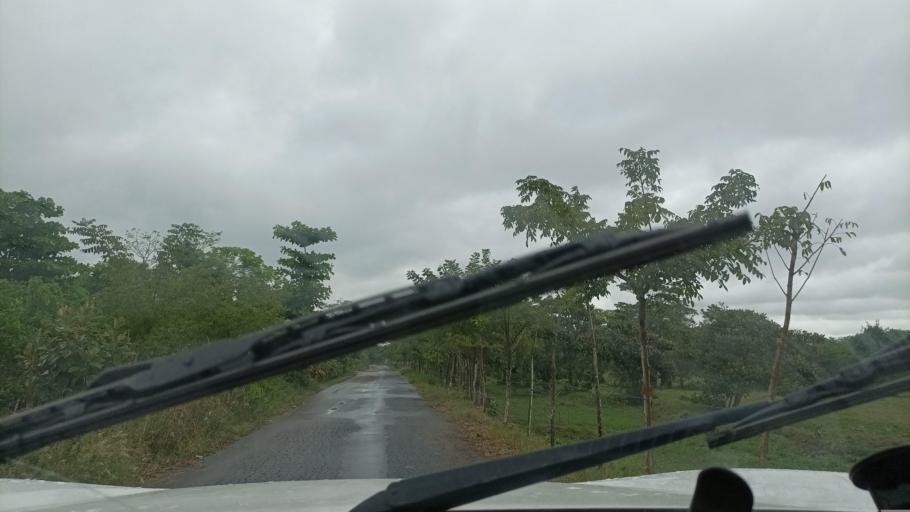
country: MX
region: Veracruz
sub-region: Moloacan
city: Cuichapa
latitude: 17.7652
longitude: -94.3892
